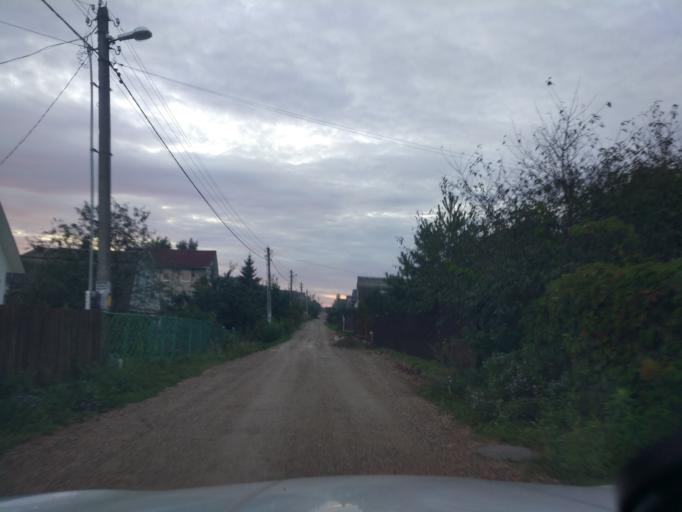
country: BY
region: Minsk
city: Astrashytski Haradok
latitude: 54.0868
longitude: 27.6997
